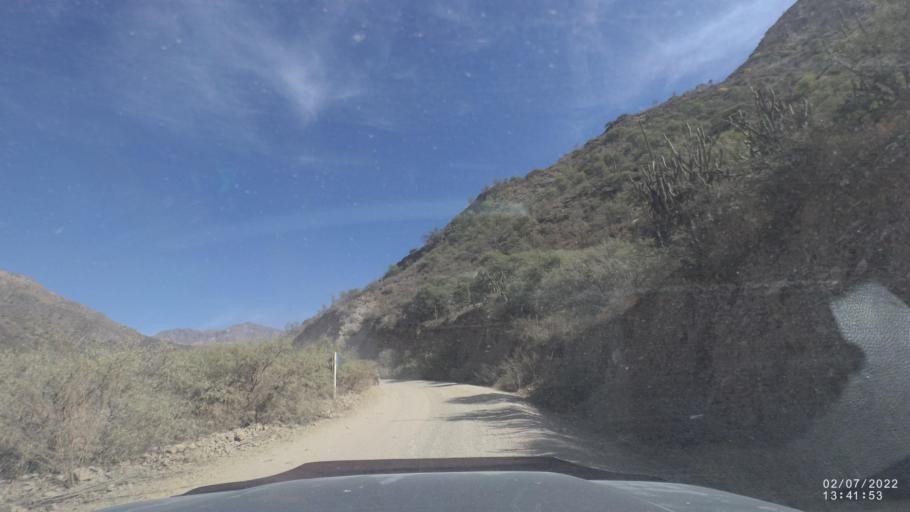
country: BO
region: Cochabamba
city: Irpa Irpa
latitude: -17.7983
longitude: -66.3540
